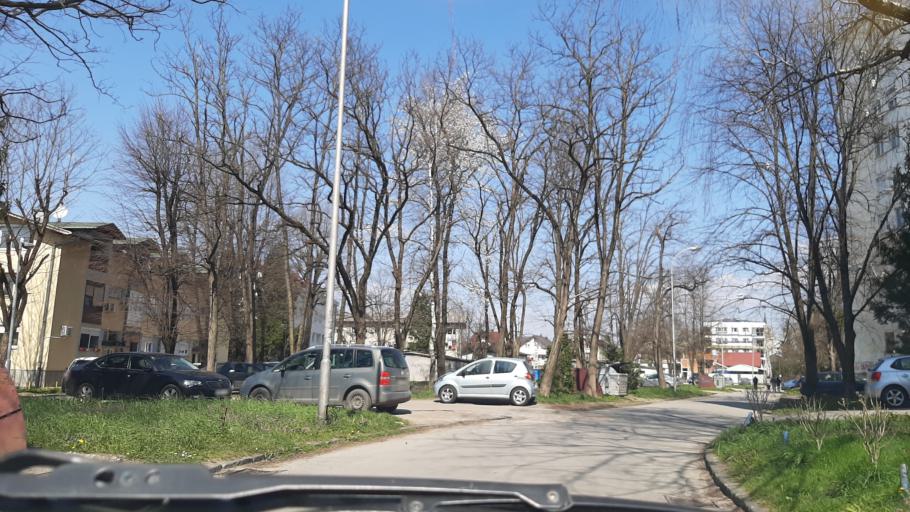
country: BA
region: Republika Srpska
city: Hiseti
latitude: 44.7606
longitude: 17.1847
